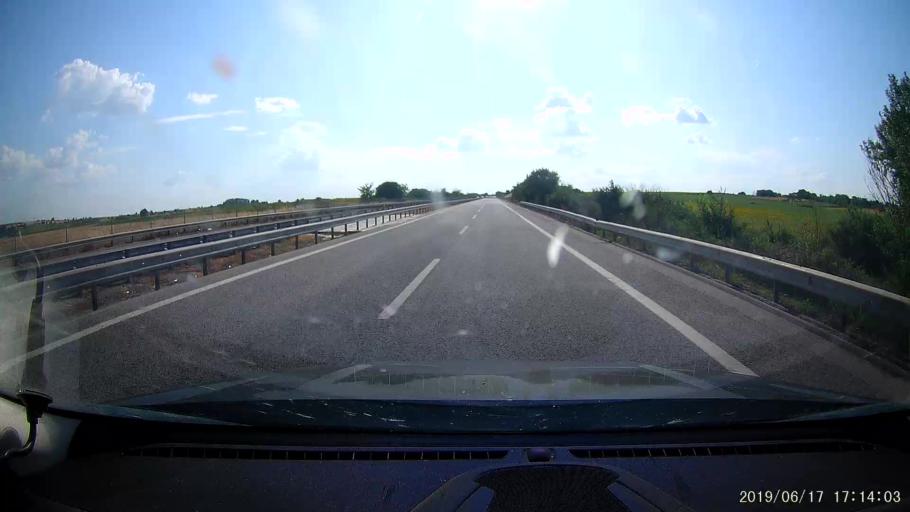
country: TR
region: Edirne
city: Edirne
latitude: 41.7000
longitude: 26.5279
